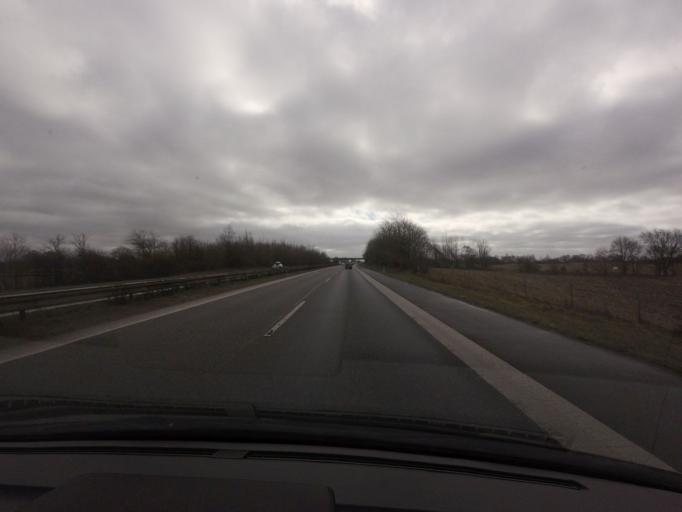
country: DE
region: Schleswig-Holstein
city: Lottorf
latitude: 54.4581
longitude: 9.5769
